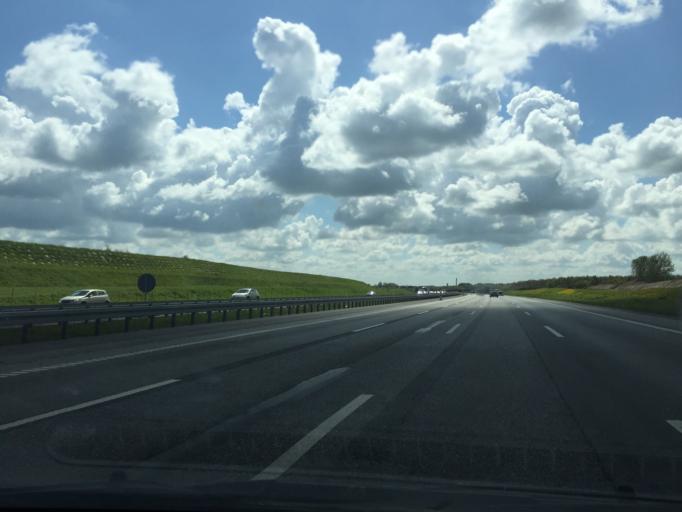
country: DK
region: Zealand
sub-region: Solrod Kommune
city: Solrod Strand
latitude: 55.5678
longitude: 12.2373
